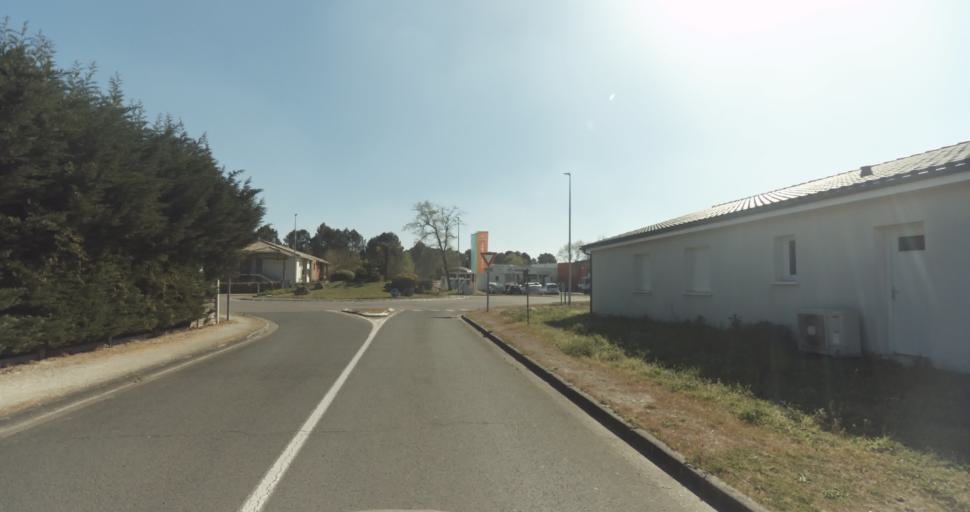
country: FR
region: Aquitaine
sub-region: Departement de la Gironde
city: Martignas-sur-Jalle
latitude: 44.8004
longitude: -0.7786
